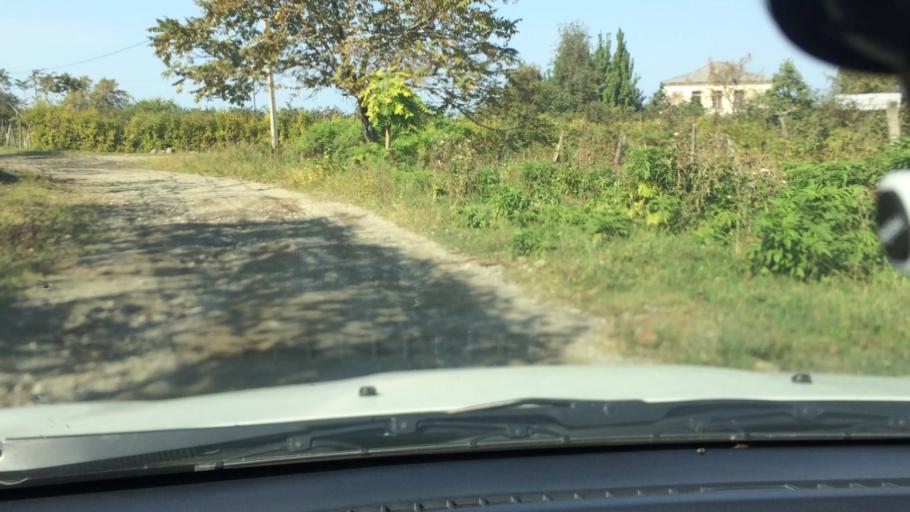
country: GE
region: Ajaria
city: Kobuleti
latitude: 41.8096
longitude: 41.8198
